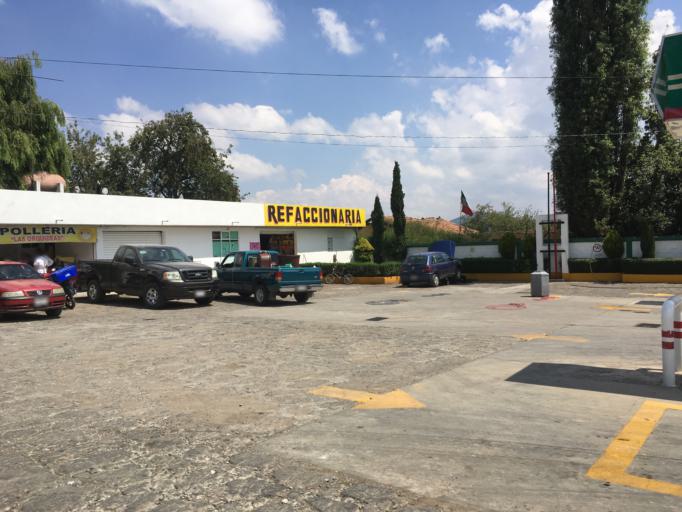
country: MX
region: Mexico
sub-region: Atlacomulco
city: Santiago Acutzilapan
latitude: 19.7914
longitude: -99.7619
